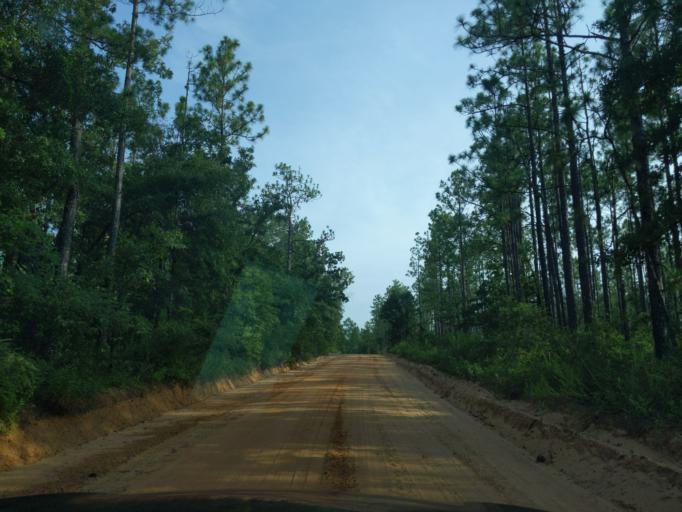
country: US
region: Florida
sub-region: Gadsden County
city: Midway
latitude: 30.3933
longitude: -84.4097
